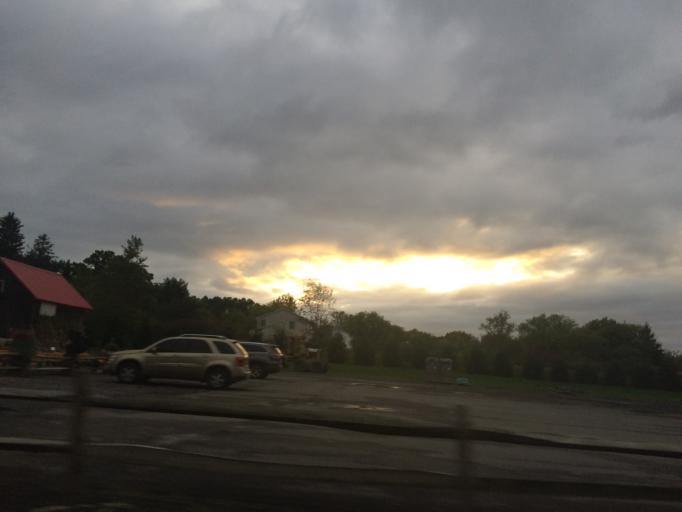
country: US
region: New York
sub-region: Erie County
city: Billington Heights
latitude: 42.7927
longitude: -78.6214
